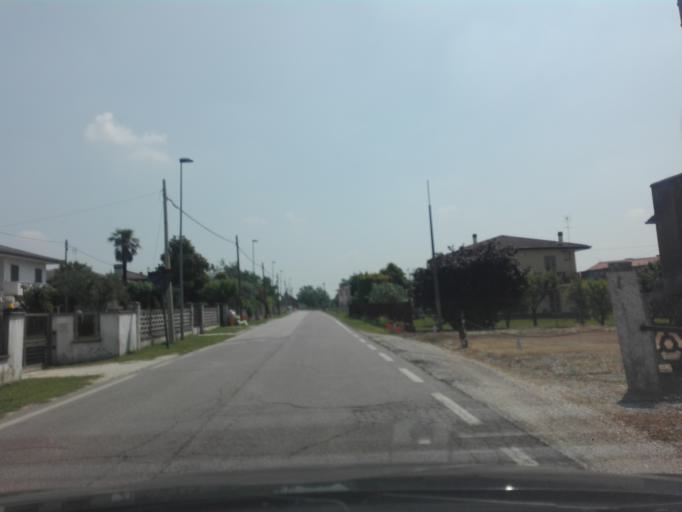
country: IT
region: Veneto
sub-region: Provincia di Rovigo
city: Lama Pezzoli
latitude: 45.0417
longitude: 11.9184
